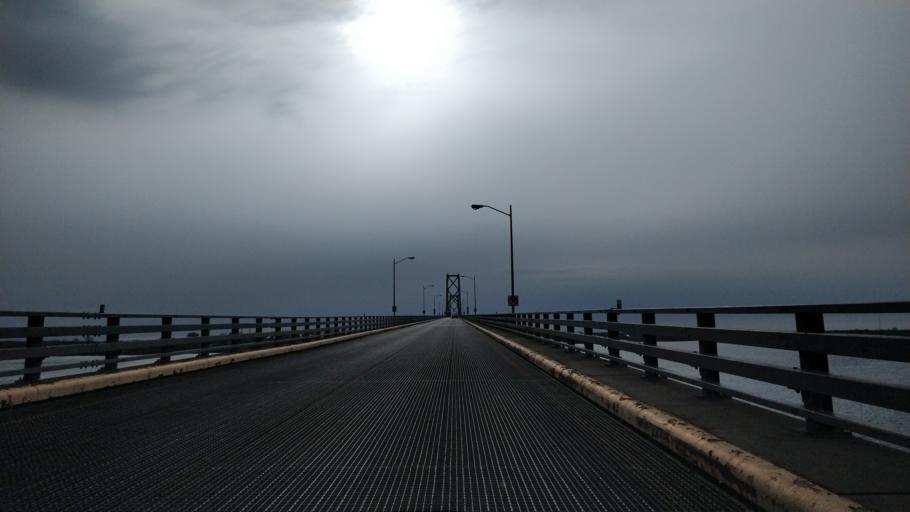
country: US
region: New York
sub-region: St. Lawrence County
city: Ogdensburg
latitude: 44.7422
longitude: -75.4649
